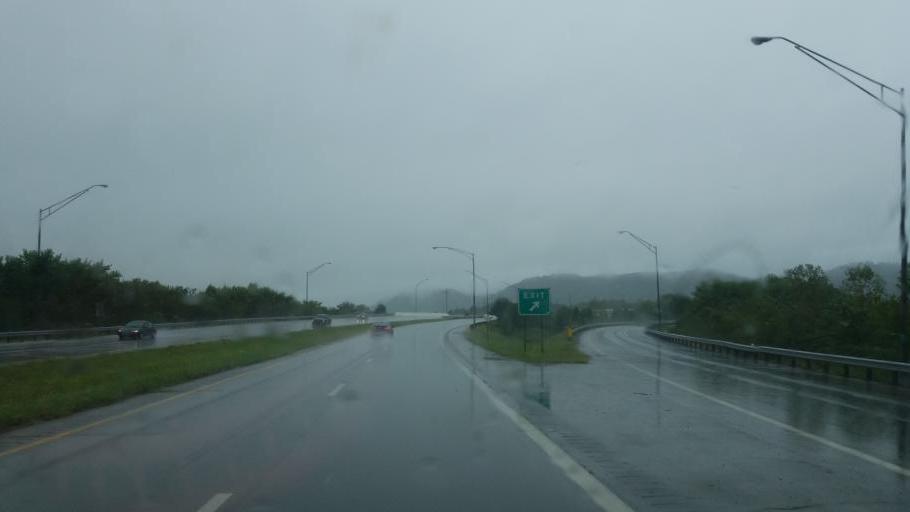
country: US
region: Ohio
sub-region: Scioto County
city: Portsmouth
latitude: 38.7376
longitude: -83.0145
